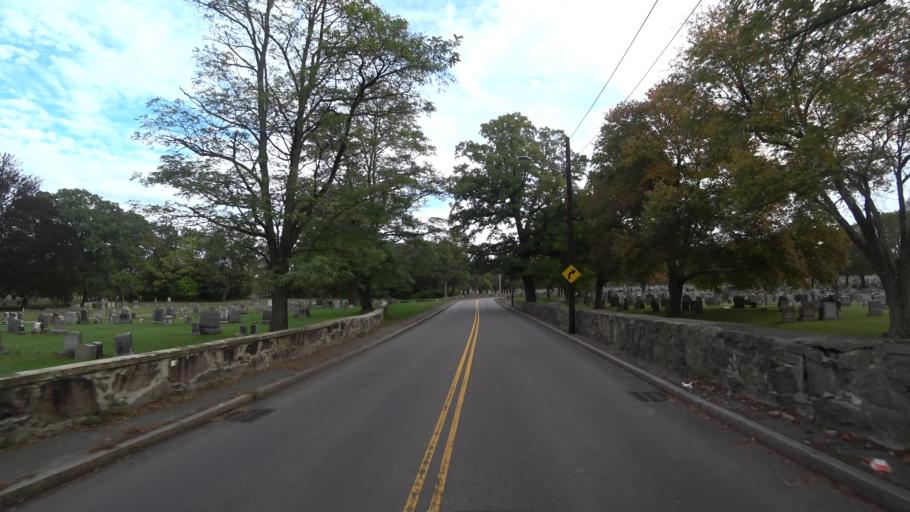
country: US
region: Massachusetts
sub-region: Suffolk County
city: Jamaica Plain
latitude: 42.2797
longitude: -71.1066
